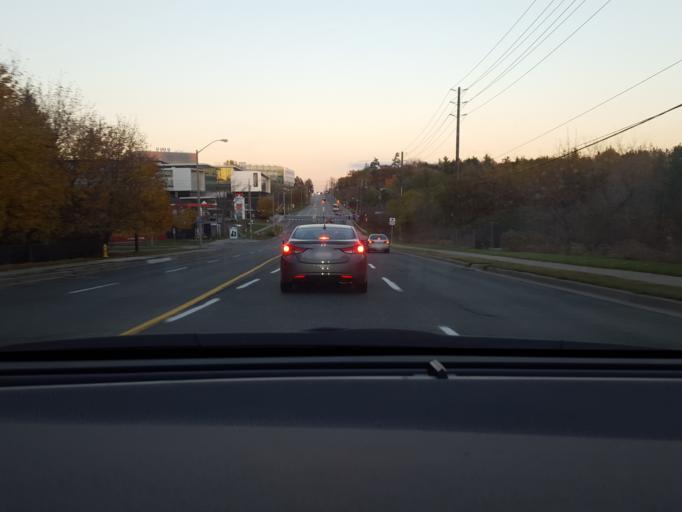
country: CA
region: Ontario
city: Scarborough
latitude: 43.7846
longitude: -79.1965
